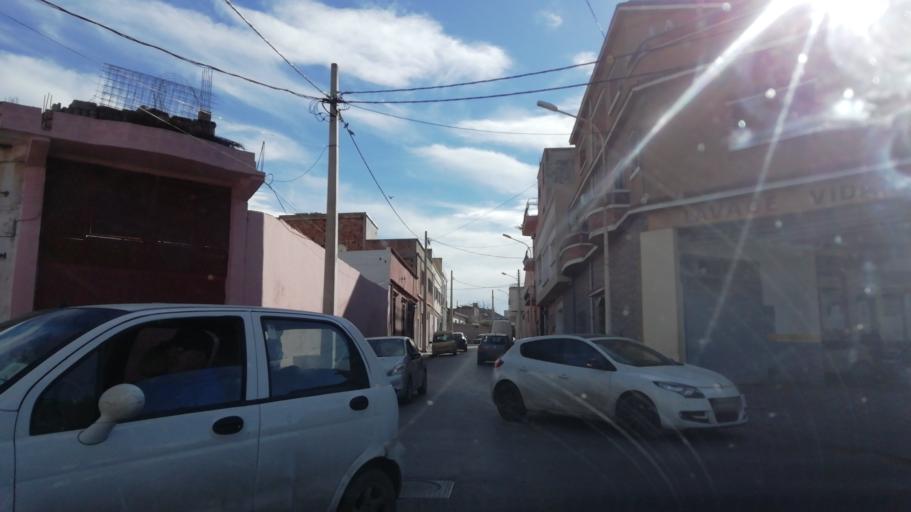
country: DZ
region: Oran
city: Oran
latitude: 35.7005
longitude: -0.6205
